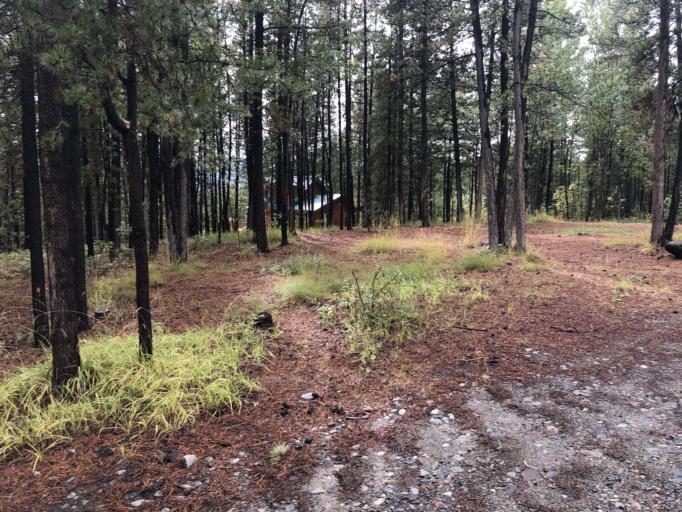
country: CA
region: Yukon
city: Whitehorse
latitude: 60.8807
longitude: -135.3573
